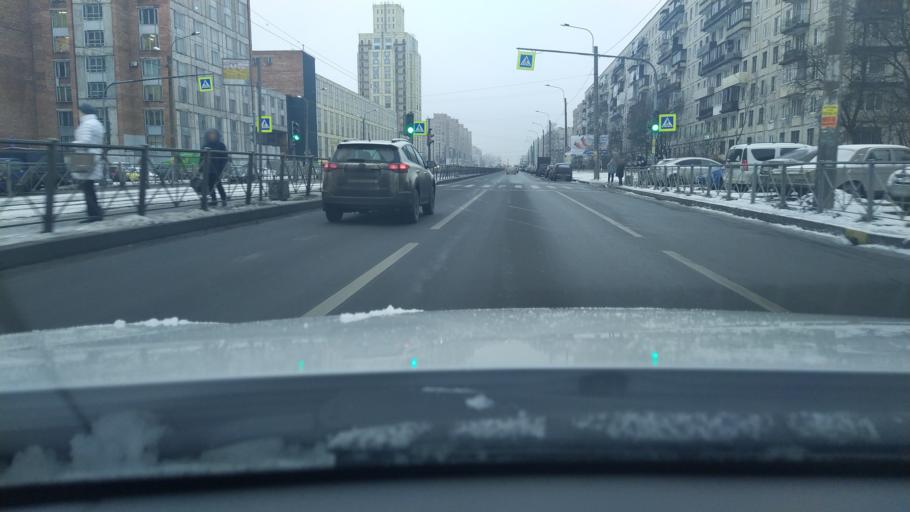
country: RU
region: St.-Petersburg
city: Grazhdanka
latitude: 60.0341
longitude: 30.4276
